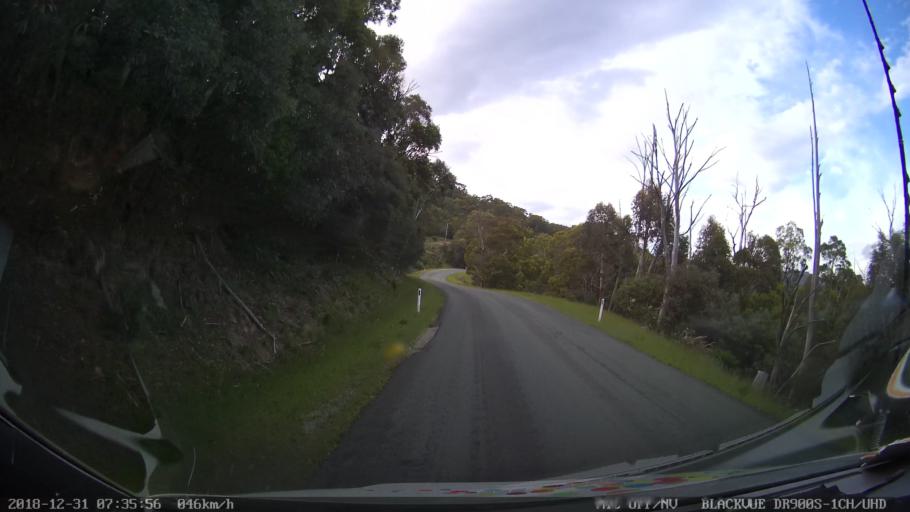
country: AU
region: New South Wales
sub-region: Snowy River
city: Jindabyne
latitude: -36.3377
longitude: 148.4439
